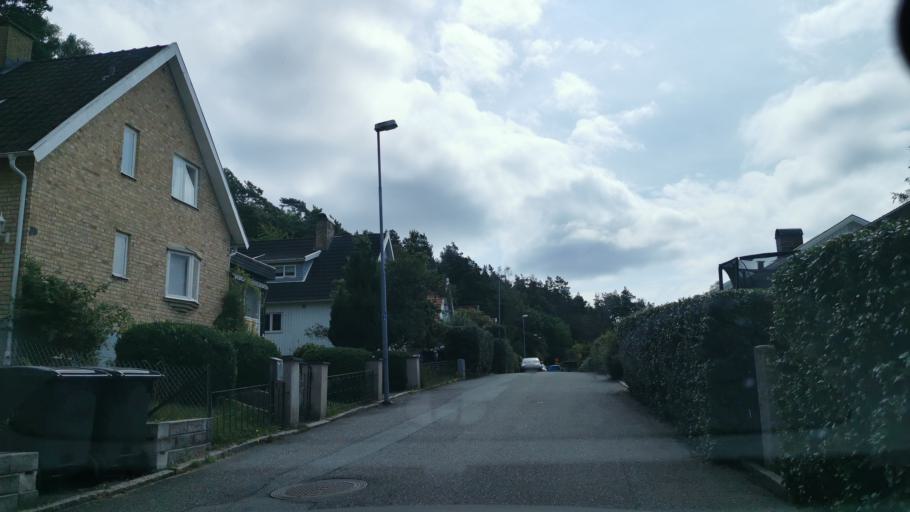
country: SE
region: Vaestra Goetaland
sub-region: Molndal
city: Moelndal
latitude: 57.6668
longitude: 11.9947
